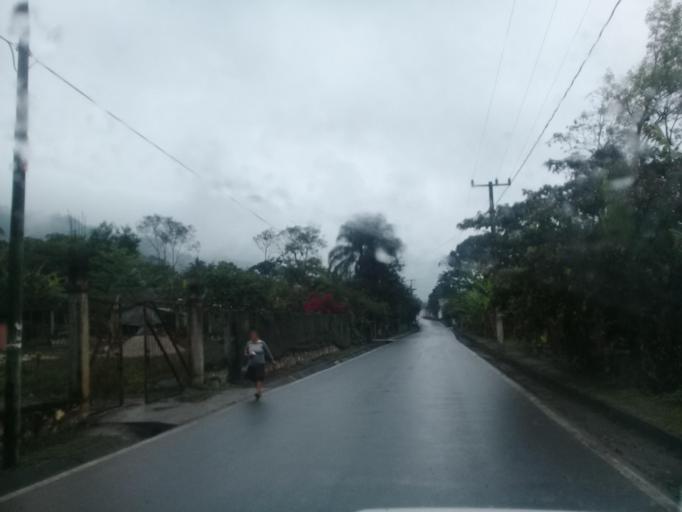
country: MX
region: Veracruz
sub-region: Amatlan de los Reyes
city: Centro de Readaptacion Social
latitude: 18.8047
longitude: -96.9542
